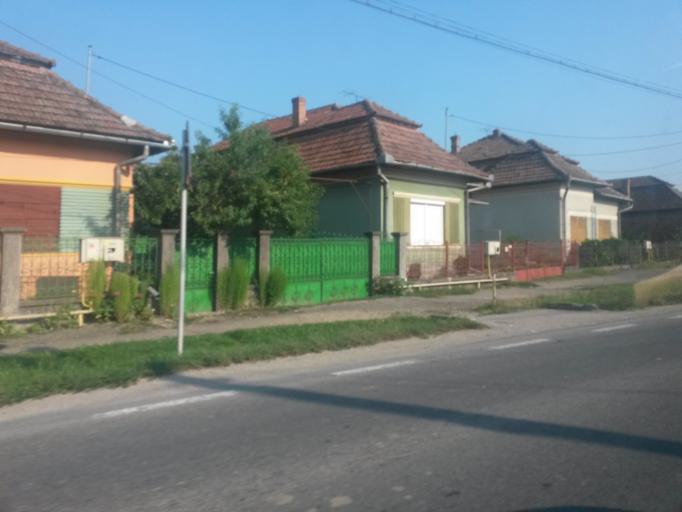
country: RO
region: Alba
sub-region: Comuna Unirea
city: Unirea
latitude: 46.3988
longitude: 23.8092
